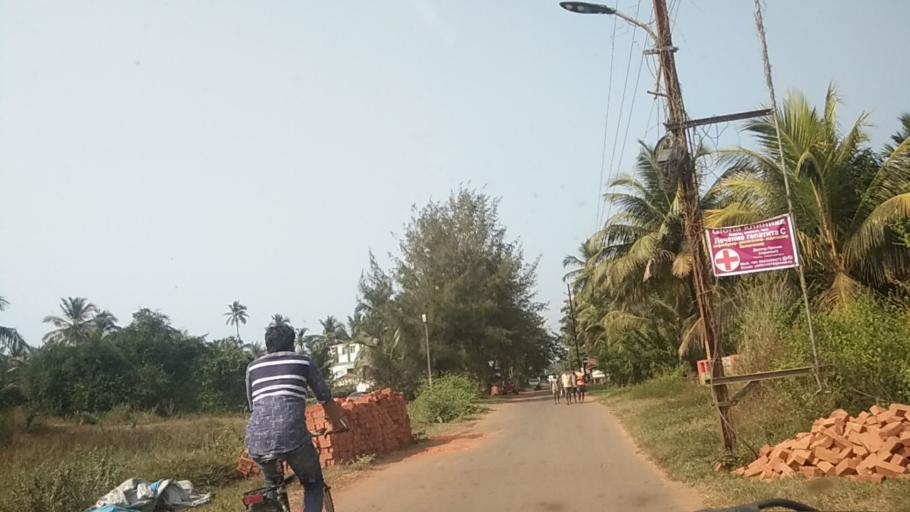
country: IN
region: Goa
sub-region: South Goa
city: Colva
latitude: 15.2831
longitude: 73.9132
